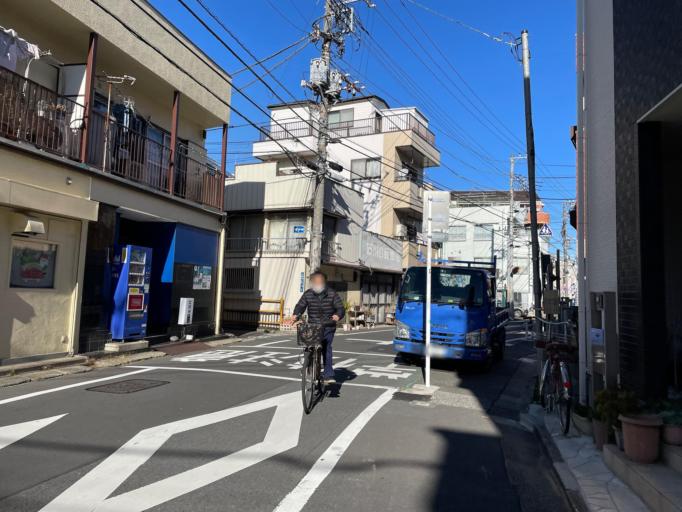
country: JP
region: Saitama
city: Soka
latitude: 35.7309
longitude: 139.8153
